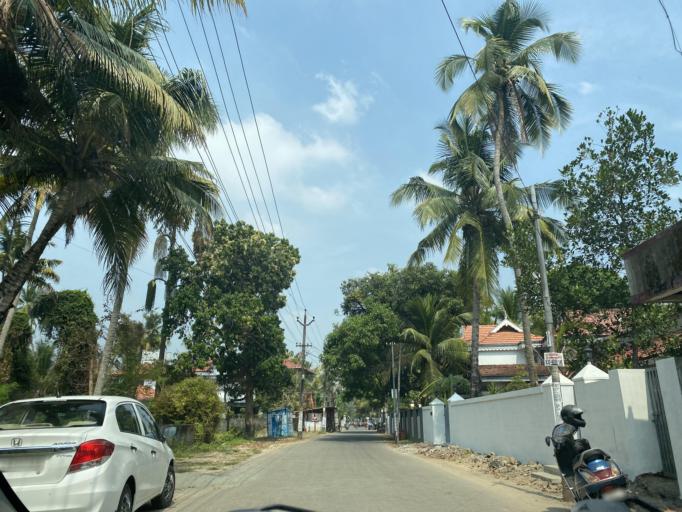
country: IN
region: Kerala
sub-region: Ernakulam
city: Cochin
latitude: 9.9377
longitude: 76.3087
